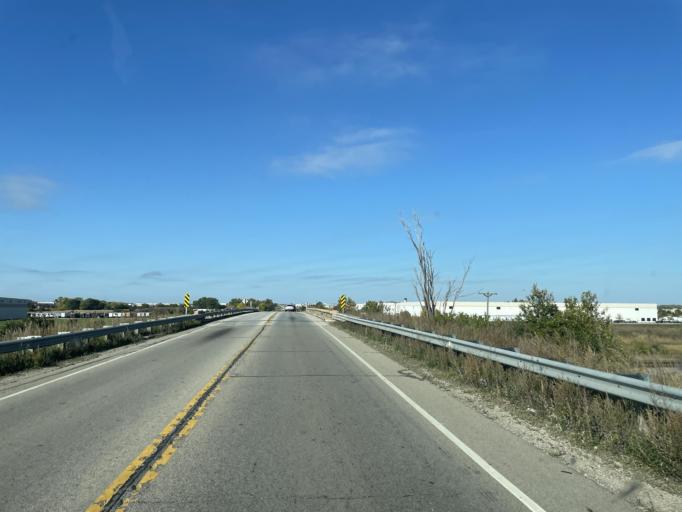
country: US
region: Wisconsin
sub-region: Kenosha County
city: Pleasant Prairie
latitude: 42.5889
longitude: -87.9040
